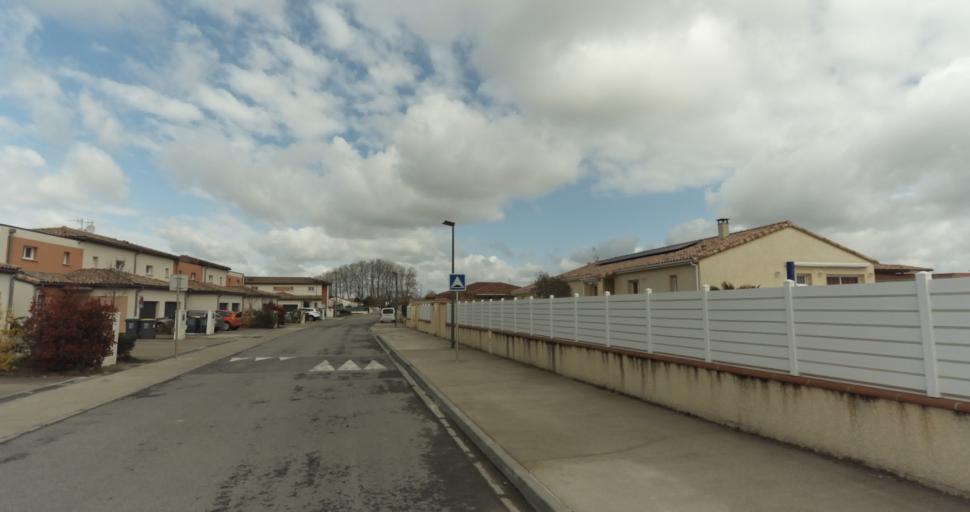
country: FR
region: Midi-Pyrenees
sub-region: Departement de la Haute-Garonne
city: Auterive
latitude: 43.3482
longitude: 1.4623
